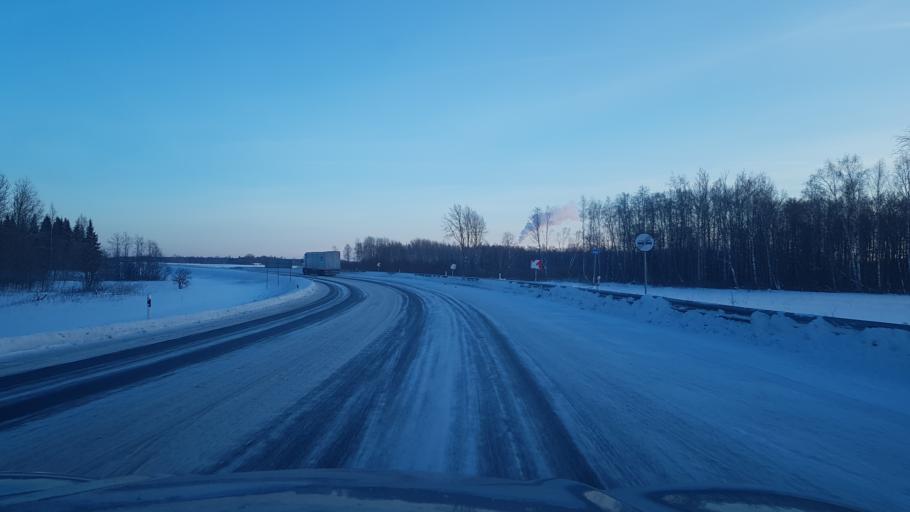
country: EE
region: Ida-Virumaa
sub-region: Narva-Joesuu linn
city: Narva-Joesuu
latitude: 59.3955
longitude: 28.0790
